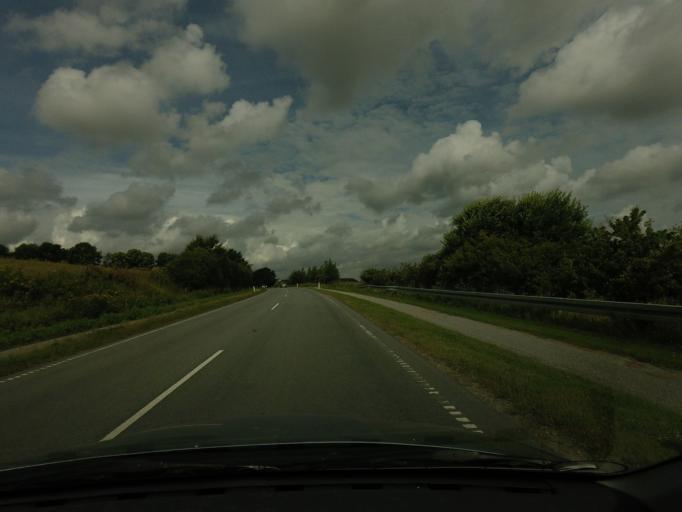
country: DK
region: North Denmark
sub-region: Hjorring Kommune
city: Tars
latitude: 57.3612
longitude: 10.2028
